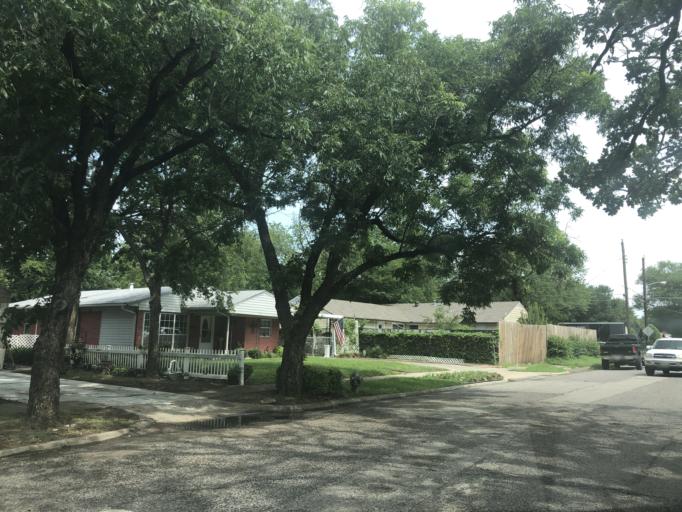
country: US
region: Texas
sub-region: Dallas County
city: Irving
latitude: 32.8070
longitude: -96.9678
